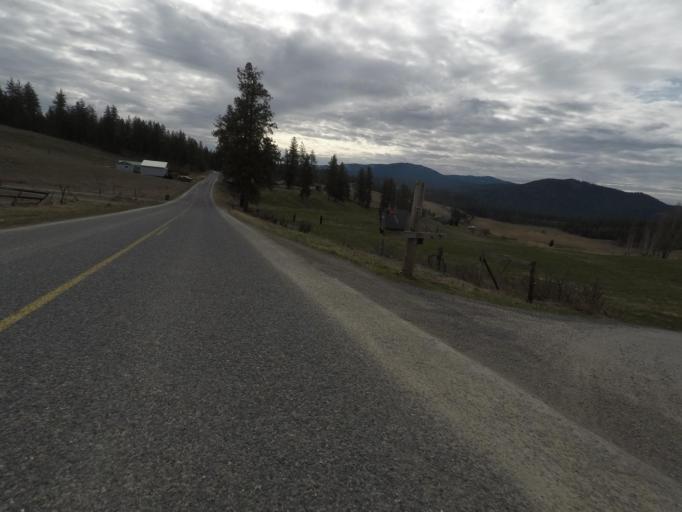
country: US
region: Washington
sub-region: Stevens County
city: Colville
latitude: 48.4999
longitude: -117.8444
